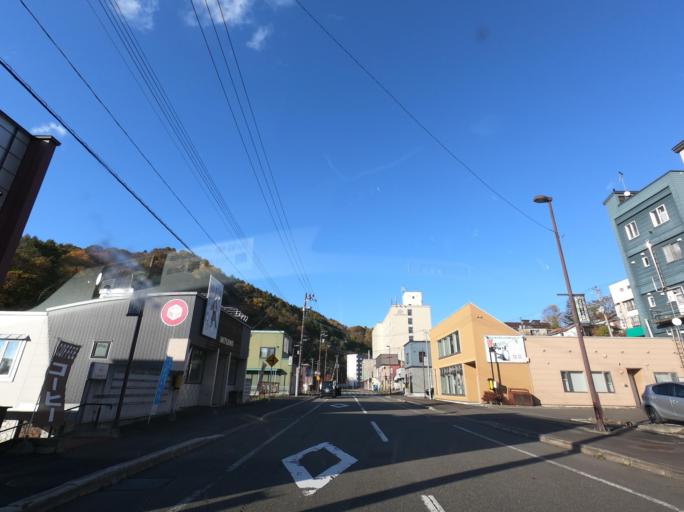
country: JP
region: Hokkaido
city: Iwamizawa
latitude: 43.0581
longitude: 141.9766
